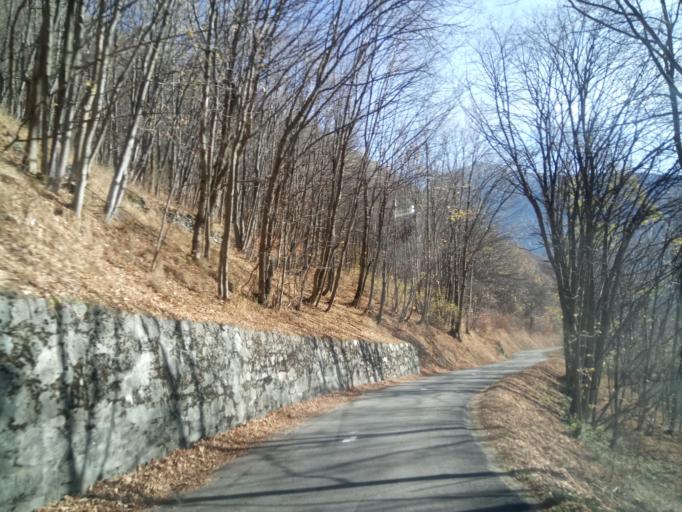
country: FR
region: Rhone-Alpes
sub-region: Departement de la Savoie
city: Saint-Michel-de-Maurienne
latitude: 45.2290
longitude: 6.4801
